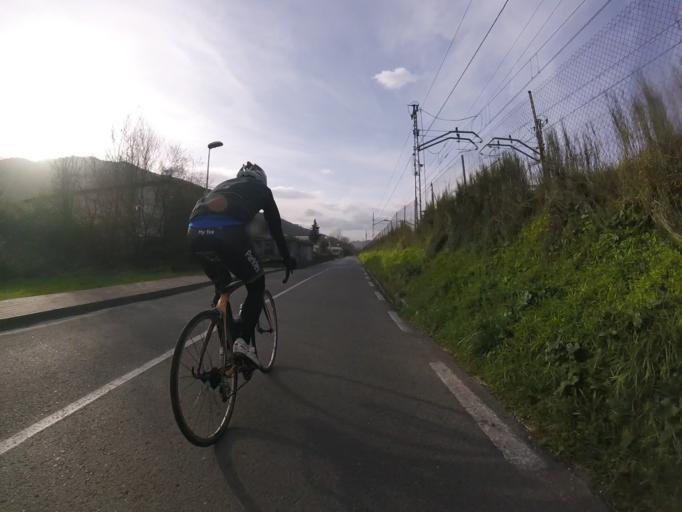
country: ES
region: Basque Country
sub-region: Provincia de Guipuzcoa
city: Villabona
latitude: 43.1827
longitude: -2.0564
